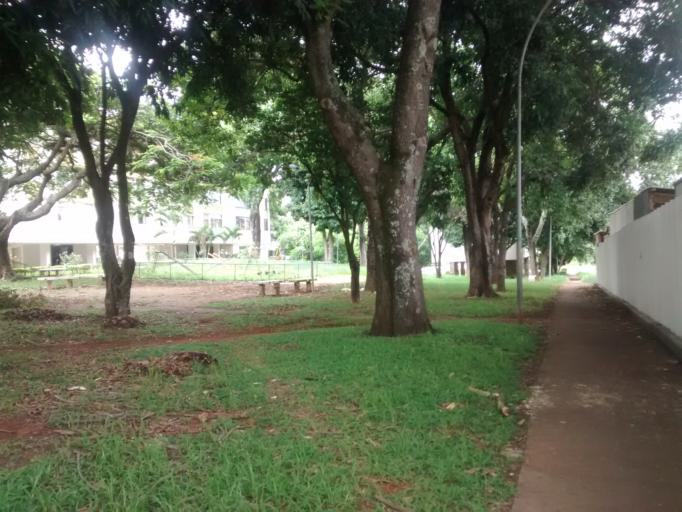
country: BR
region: Federal District
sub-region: Brasilia
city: Brasilia
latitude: -15.7478
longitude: -47.8832
